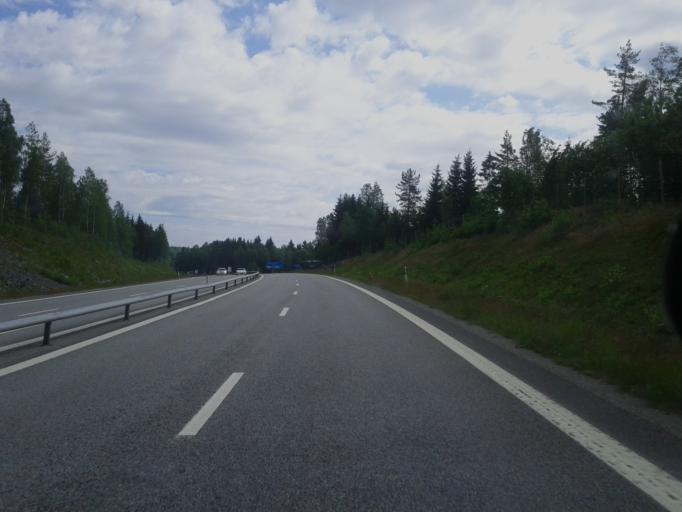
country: SE
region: Vaesternorrland
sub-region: OErnskoeldsviks Kommun
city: Ornskoldsvik
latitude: 63.2961
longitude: 18.8755
